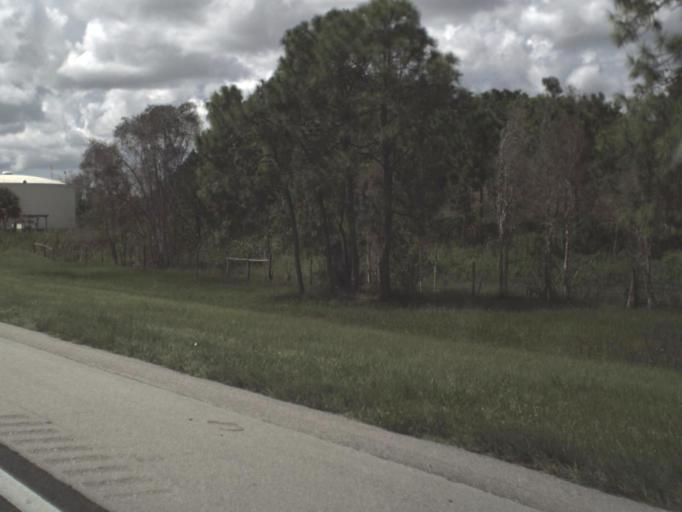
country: US
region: Florida
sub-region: Lee County
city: Bonita Springs
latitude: 26.3903
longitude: -81.7729
